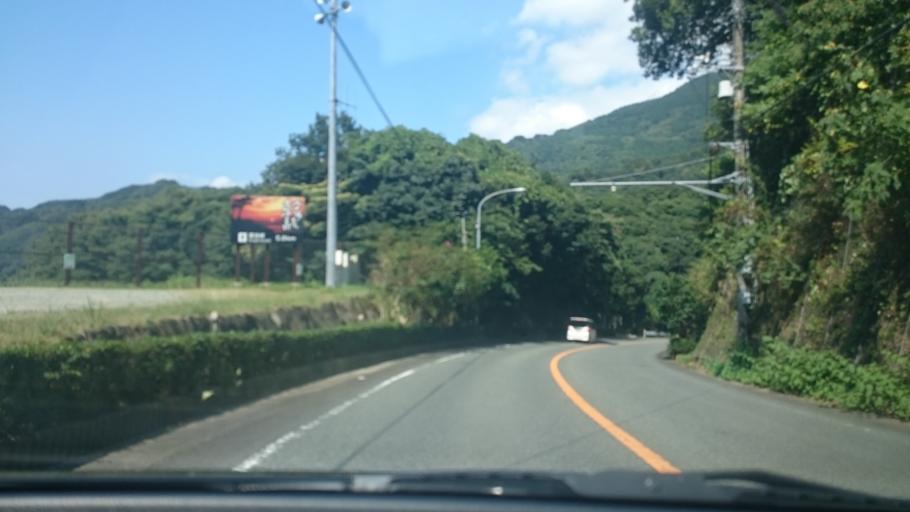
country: JP
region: Shizuoka
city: Heda
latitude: 34.8049
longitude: 138.7727
